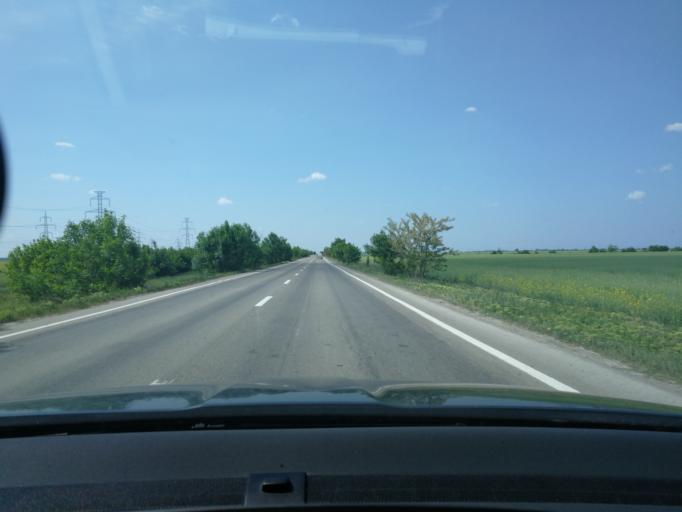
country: RO
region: Prahova
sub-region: Comuna Targsoru Vechi
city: Strejnicu
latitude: 44.8910
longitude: 25.9598
